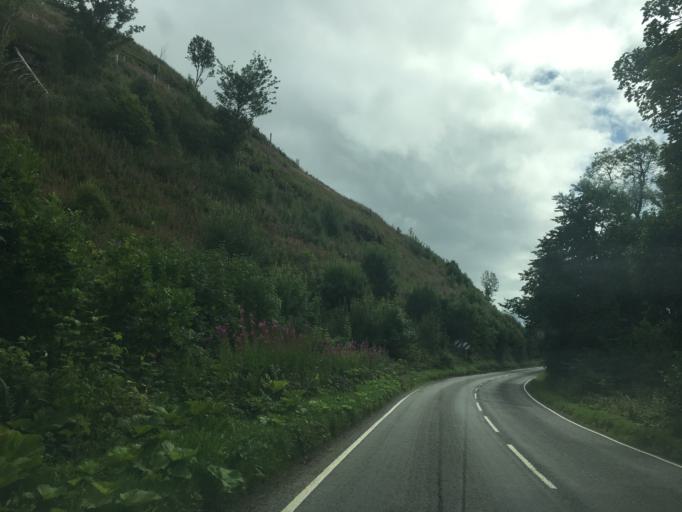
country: GB
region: Scotland
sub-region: Argyll and Bute
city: Lochgilphead
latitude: 56.1321
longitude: -5.4838
